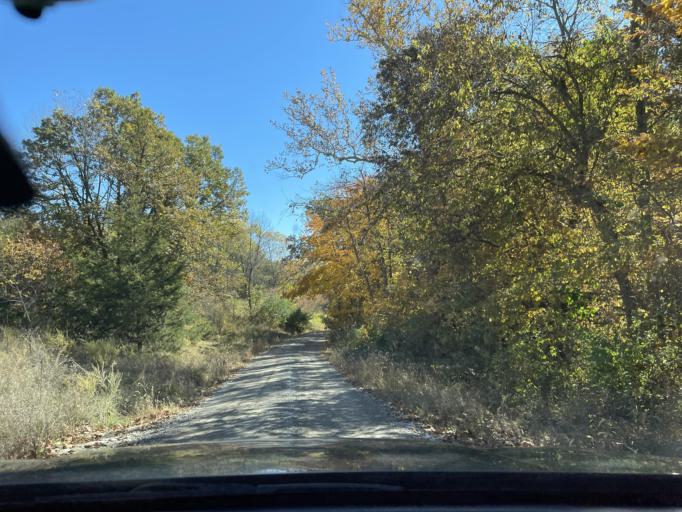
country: US
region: Missouri
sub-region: Andrew County
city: Savannah
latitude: 39.9378
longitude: -94.8670
